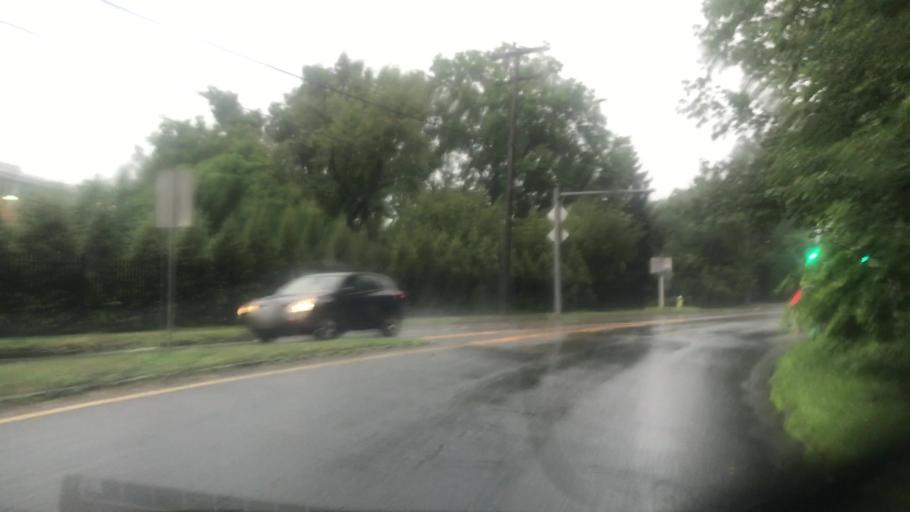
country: US
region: Connecticut
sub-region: Fairfield County
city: Byram
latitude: 41.0102
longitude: -73.6456
